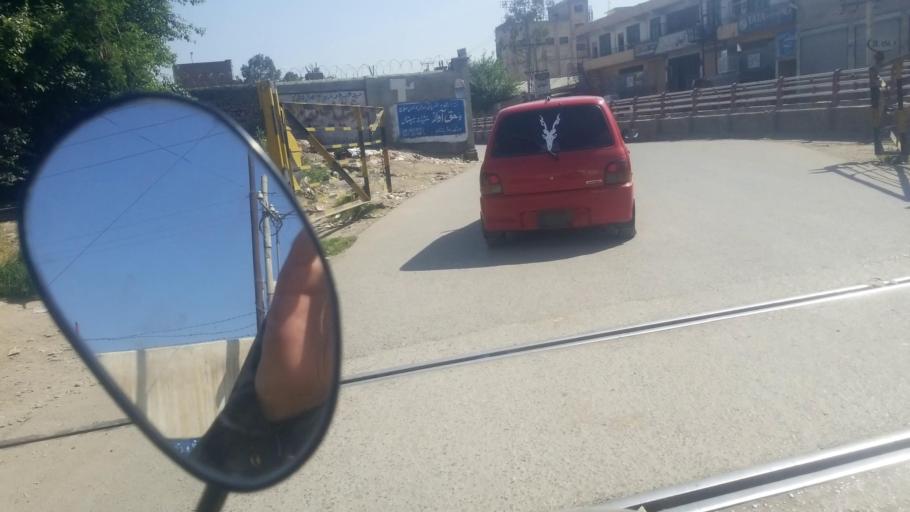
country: PK
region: Khyber Pakhtunkhwa
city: Peshawar
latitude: 34.0181
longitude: 71.5928
